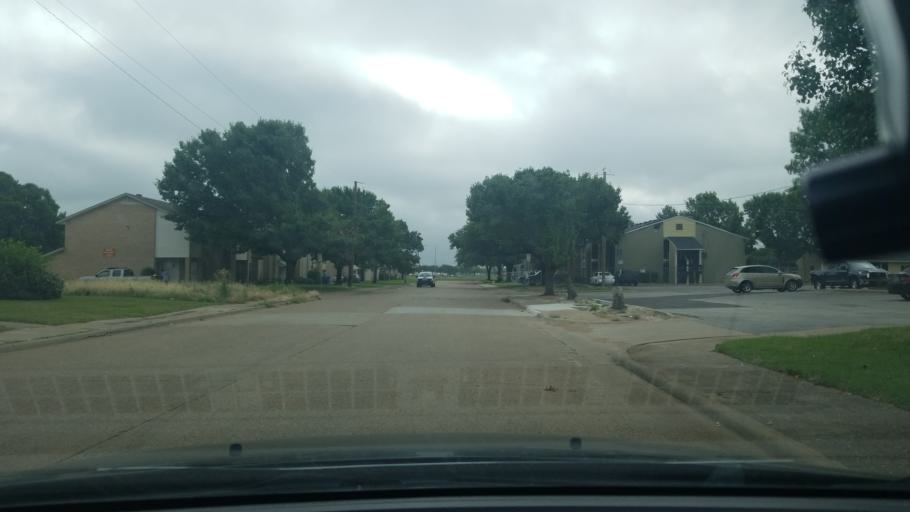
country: US
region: Texas
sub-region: Dallas County
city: Balch Springs
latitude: 32.7831
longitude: -96.6861
